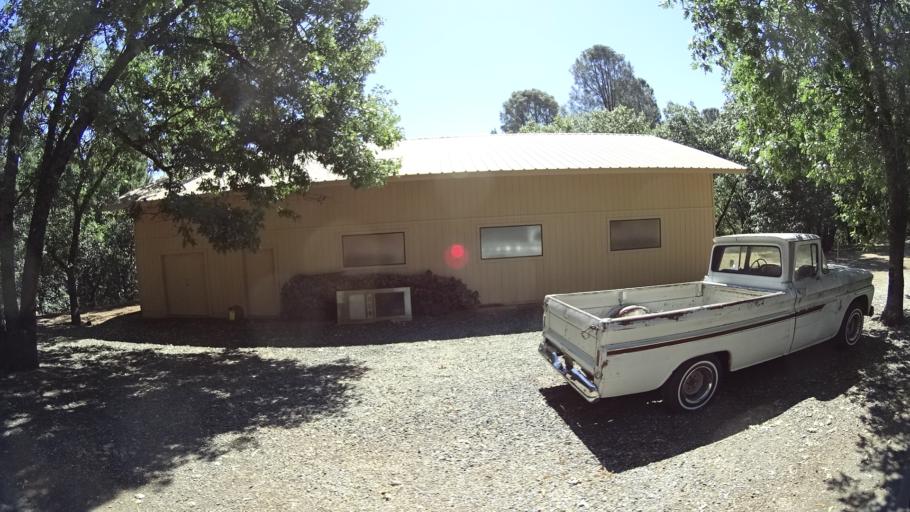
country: US
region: California
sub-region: Calaveras County
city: Forest Meadows
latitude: 38.1708
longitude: -120.3770
